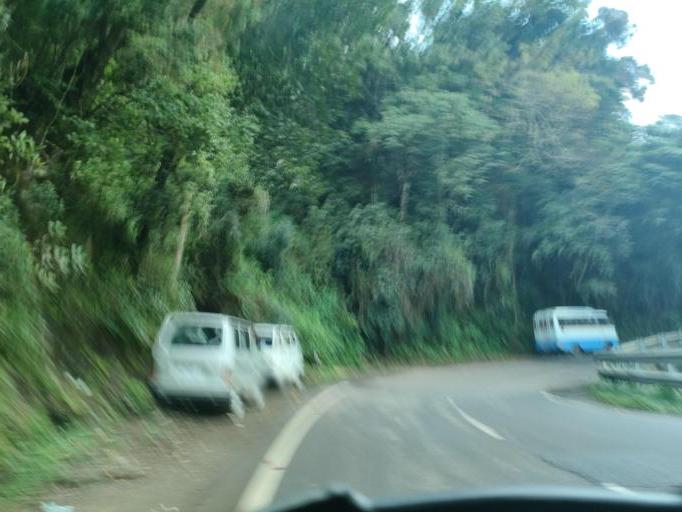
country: IN
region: Tamil Nadu
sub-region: Dindigul
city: Kodaikanal
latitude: 10.2565
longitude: 77.5310
